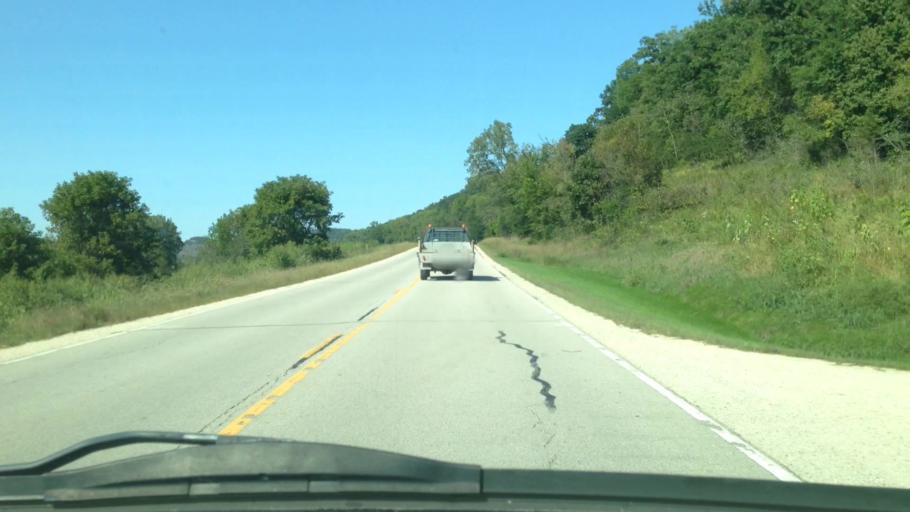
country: US
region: Minnesota
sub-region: Fillmore County
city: Rushford
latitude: 43.7732
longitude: -91.7635
